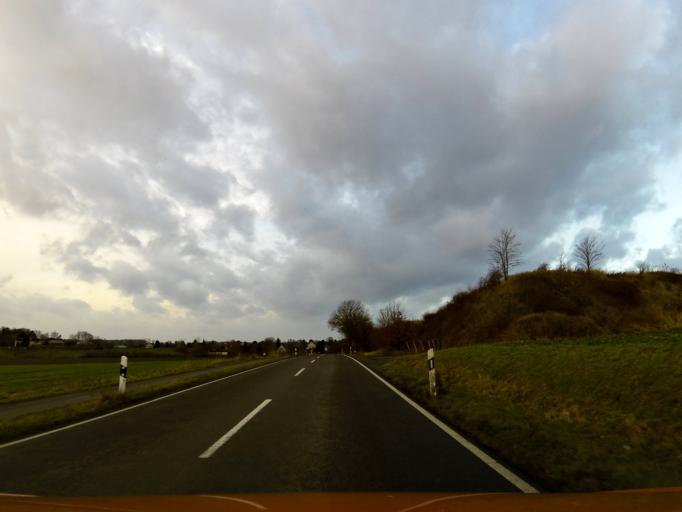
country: DE
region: Lower Saxony
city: Gross Twulpstedt
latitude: 52.3771
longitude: 10.9108
